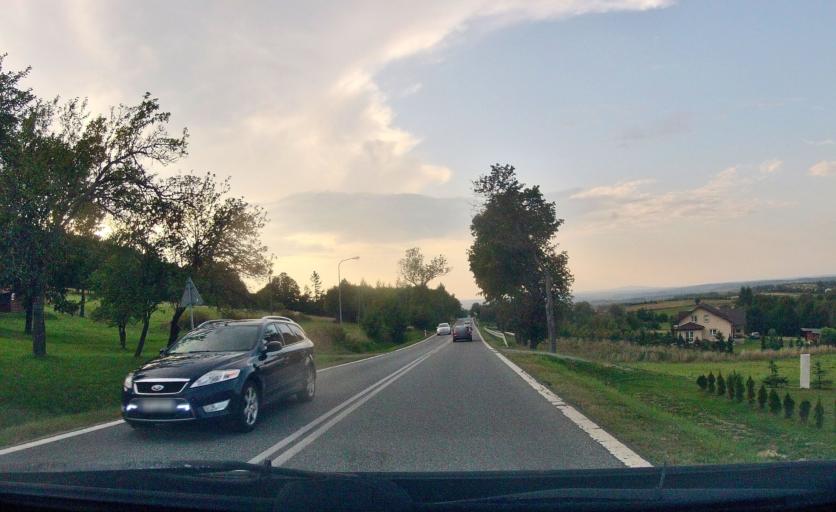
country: PL
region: Subcarpathian Voivodeship
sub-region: Powiat jasielski
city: Nowy Zmigrod
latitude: 49.5718
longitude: 21.5681
